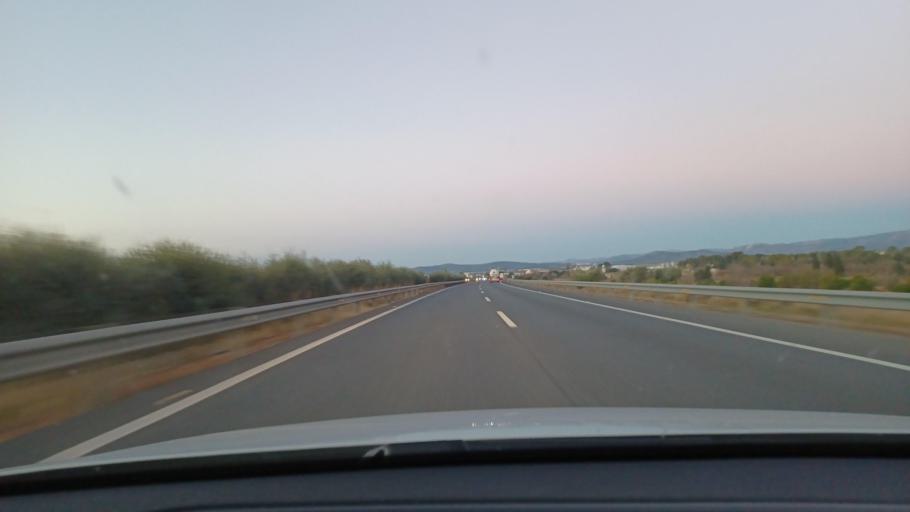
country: ES
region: Catalonia
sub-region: Provincia de Tarragona
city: Ulldecona
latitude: 40.5773
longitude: 0.4477
